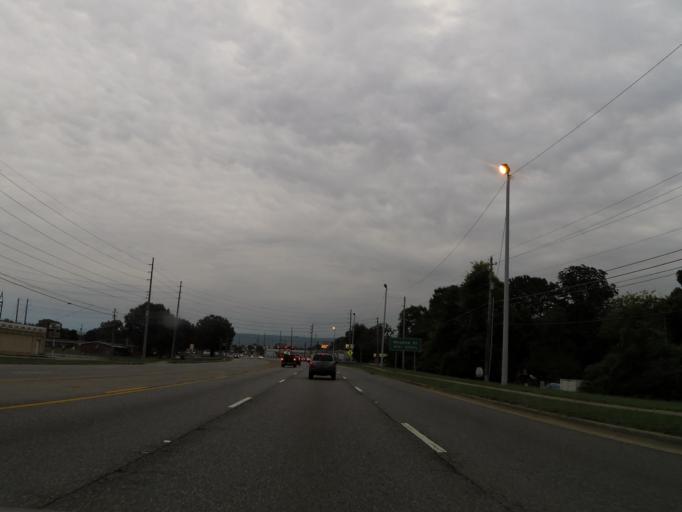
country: US
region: Alabama
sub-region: Madison County
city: Huntsville
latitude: 34.7351
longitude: -86.6148
